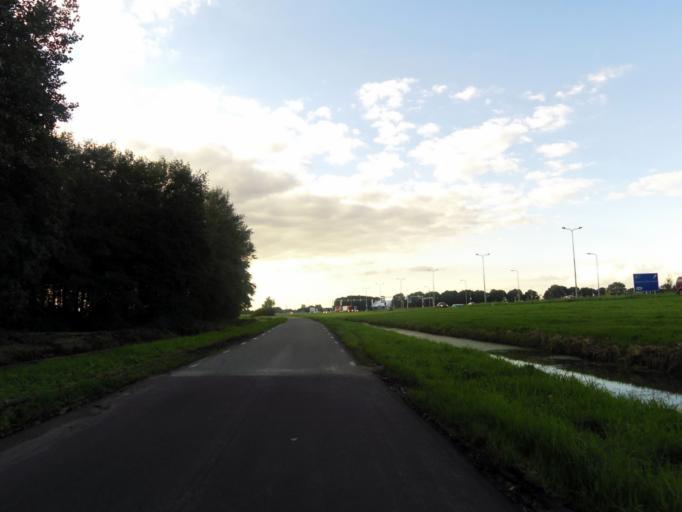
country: NL
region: South Holland
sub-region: Gemeente Alphen aan den Rijn
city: Alphen aan den Rijn
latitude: 52.1217
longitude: 4.6281
